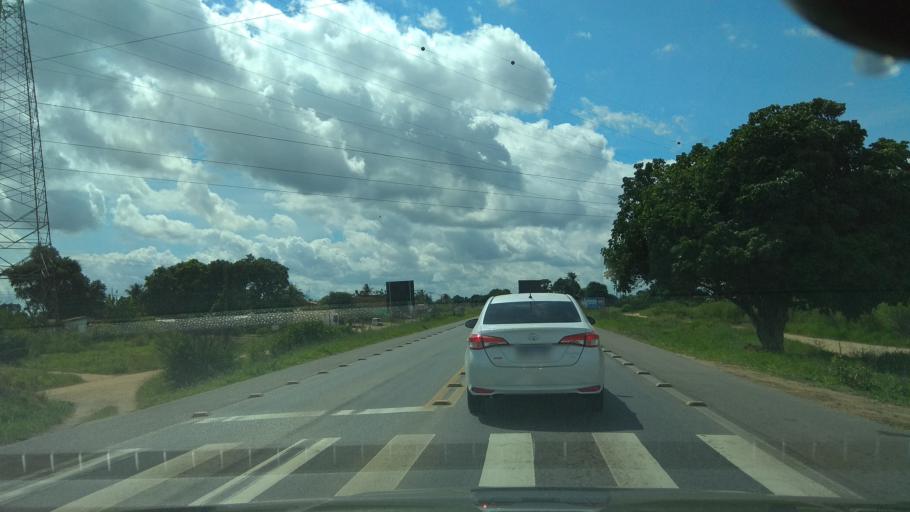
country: BR
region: Bahia
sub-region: Cruz Das Almas
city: Cruz das Almas
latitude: -12.6282
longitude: -39.0917
